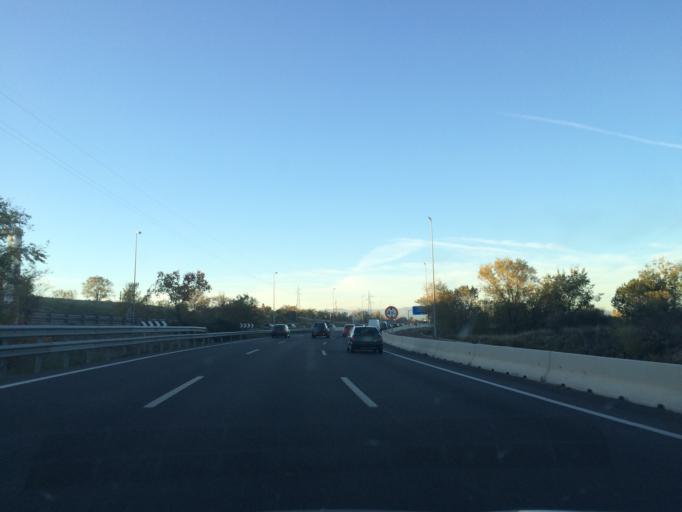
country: ES
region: Madrid
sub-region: Provincia de Madrid
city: Las Tablas
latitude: 40.5431
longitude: -3.7018
